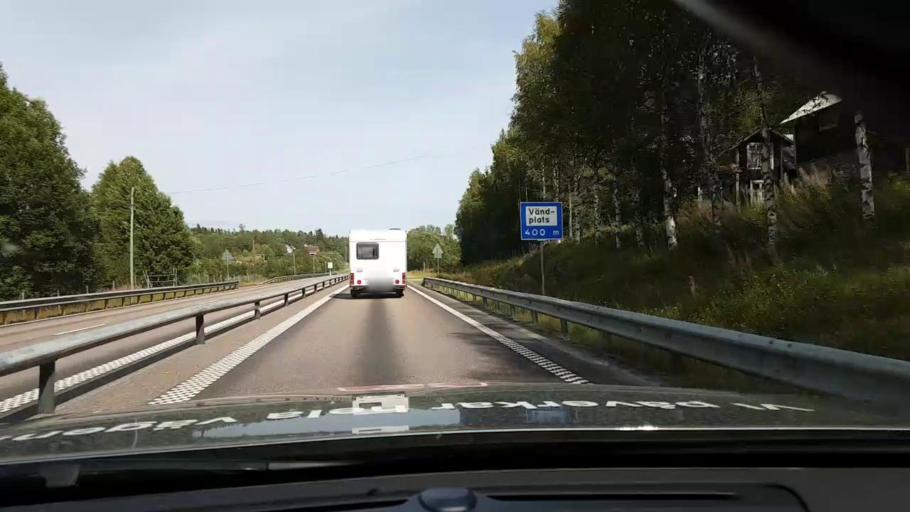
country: SE
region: Vaesternorrland
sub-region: OErnskoeldsviks Kommun
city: Husum
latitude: 63.3589
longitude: 19.1723
